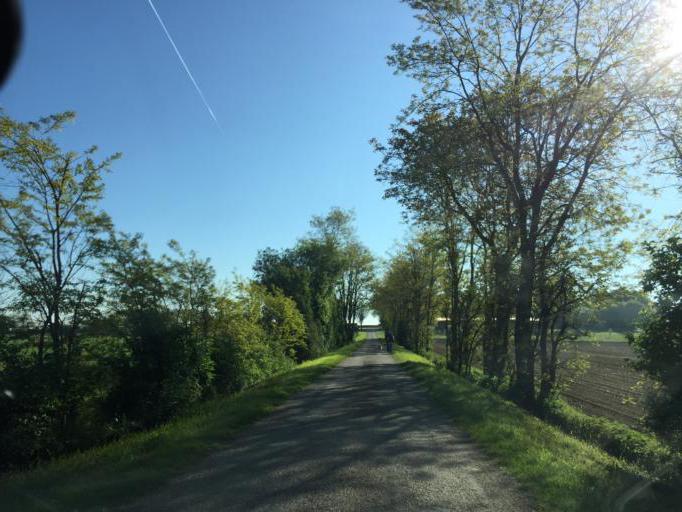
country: FR
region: Rhone-Alpes
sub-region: Departement de l'Ain
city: Saint-Maurice-de-Beynost
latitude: 45.8475
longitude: 4.9820
